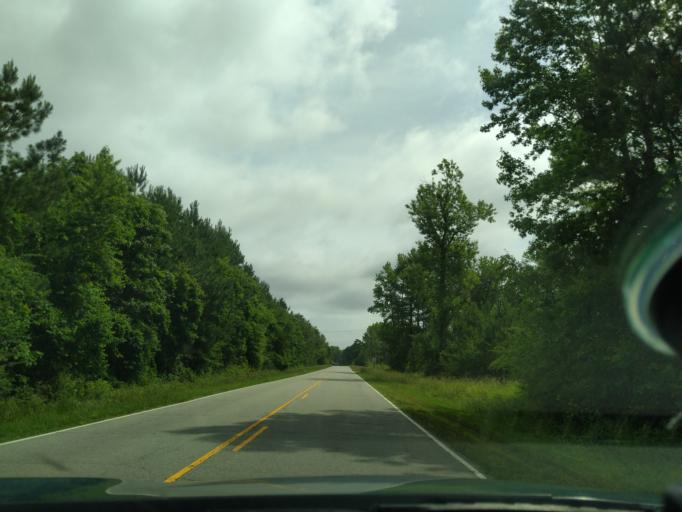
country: US
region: North Carolina
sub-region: Chowan County
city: Edenton
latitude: 35.9218
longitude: -76.5951
